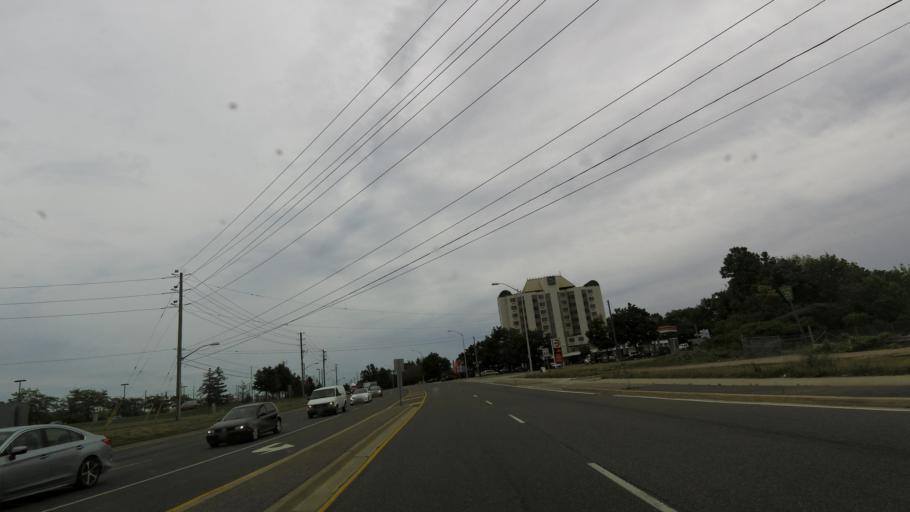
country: CA
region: Ontario
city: Oakville
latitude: 43.4087
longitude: -79.7387
